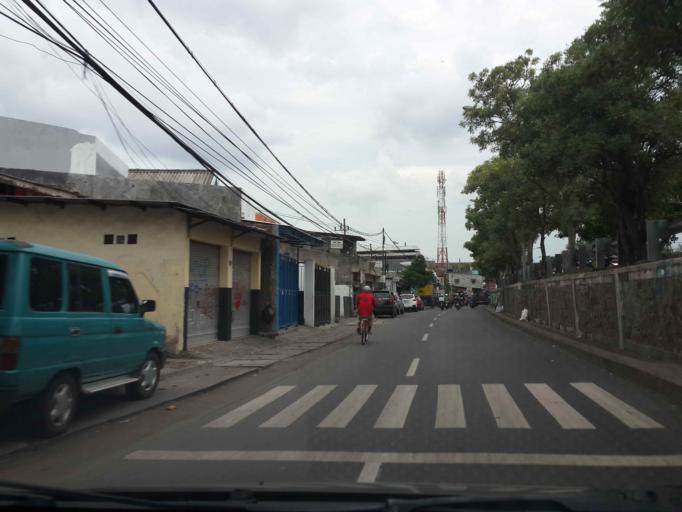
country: ID
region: East Java
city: Gubengairlangga
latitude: -7.2718
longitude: 112.7233
